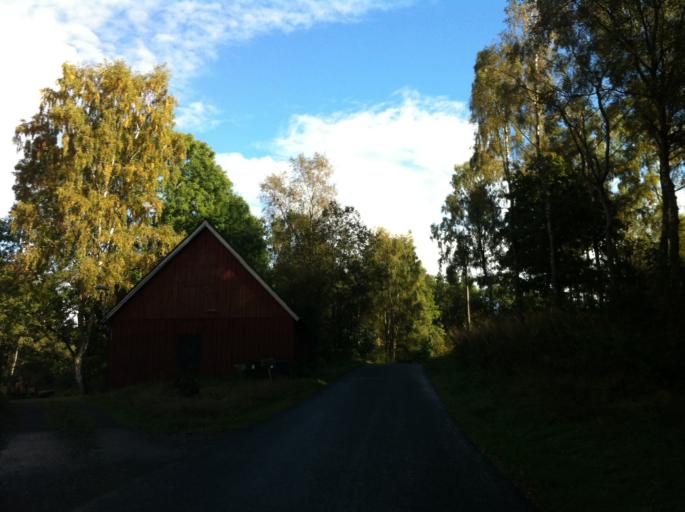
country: SE
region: Skane
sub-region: Perstorps Kommun
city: Perstorp
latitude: 56.1403
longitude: 13.5264
